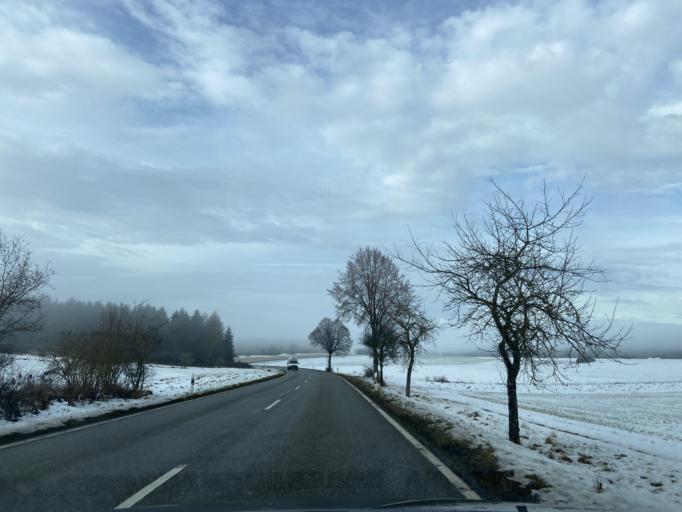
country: DE
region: Baden-Wuerttemberg
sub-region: Tuebingen Region
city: Gammertingen
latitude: 48.2407
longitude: 9.2506
